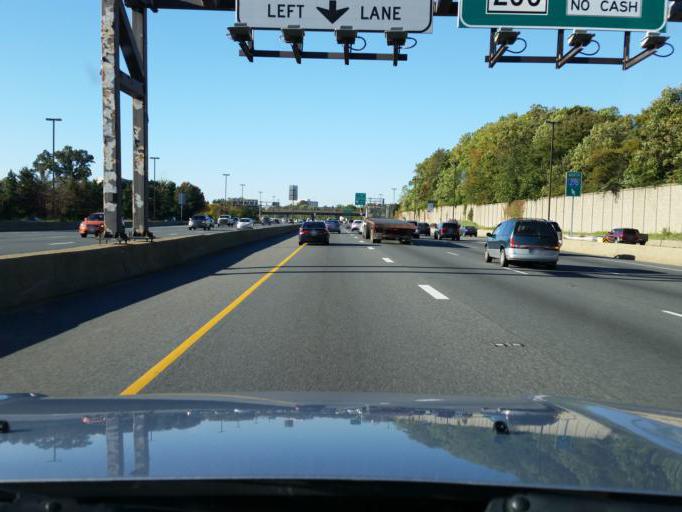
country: US
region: Maryland
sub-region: Montgomery County
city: Derwood
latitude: 39.0970
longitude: -77.1775
